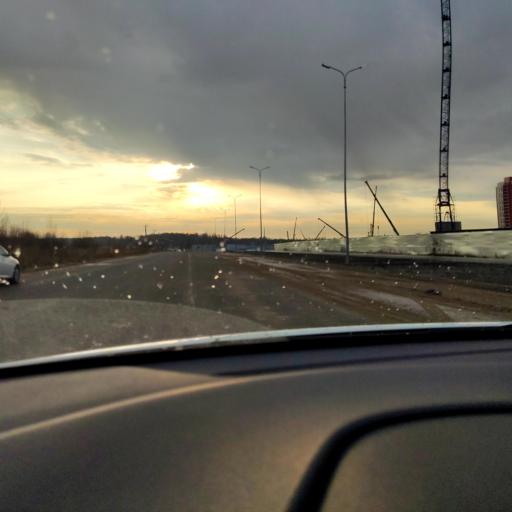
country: RU
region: Tatarstan
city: Osinovo
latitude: 55.8608
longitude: 48.9045
